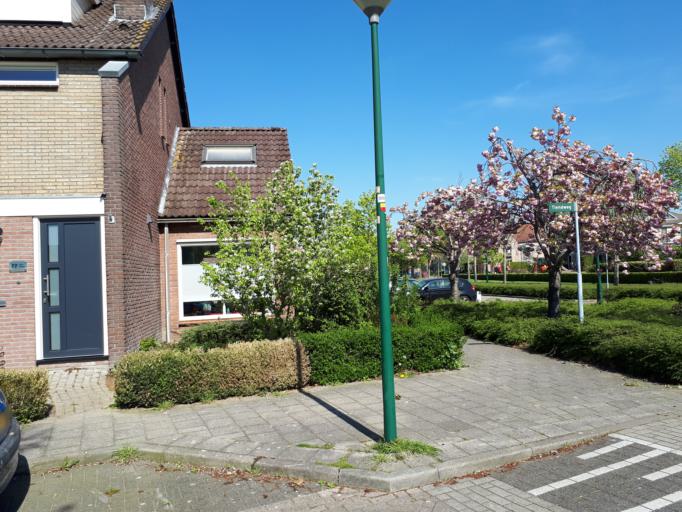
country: NL
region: Utrecht
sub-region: Gemeente Montfoort
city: Montfoort
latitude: 52.0437
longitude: 4.9576
